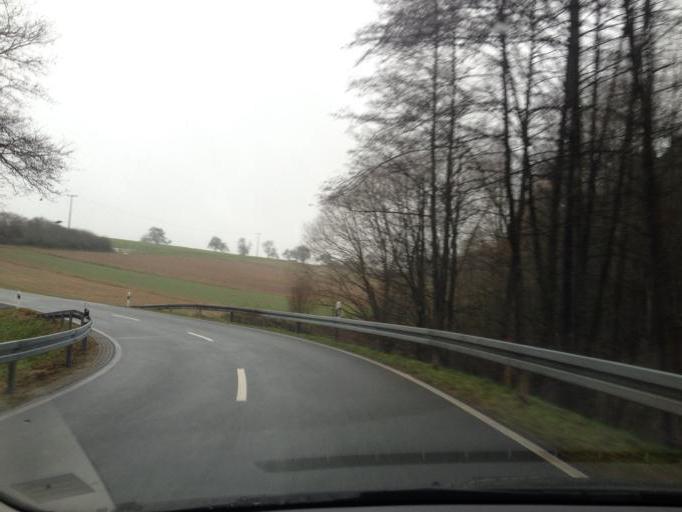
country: DE
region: Bavaria
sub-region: Regierungsbezirk Mittelfranken
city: Lauf an der Pegnitz
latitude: 49.5530
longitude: 11.2499
